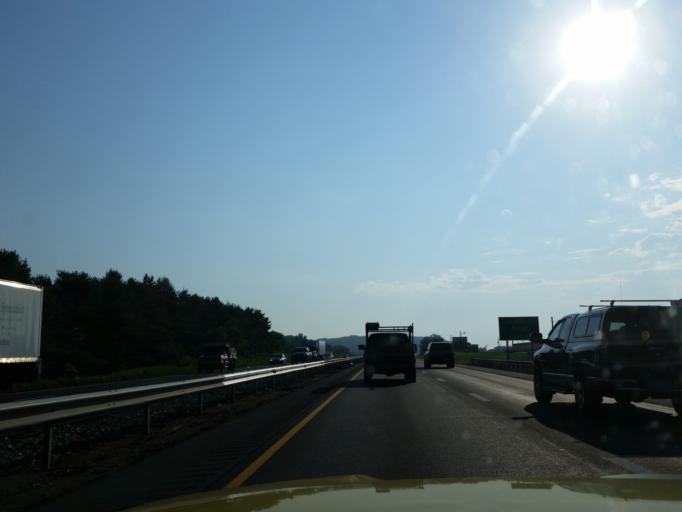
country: US
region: Pennsylvania
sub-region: Lancaster County
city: Mountville
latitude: 40.0493
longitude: -76.4051
